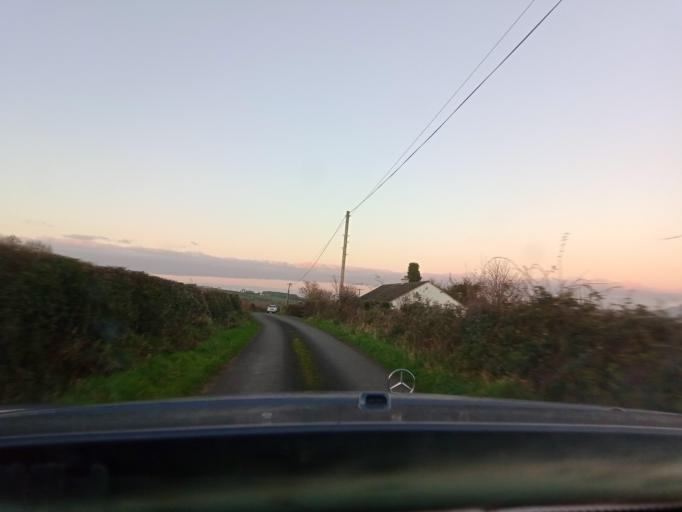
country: IE
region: Leinster
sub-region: Kilkenny
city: Graiguenamanagh
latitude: 52.5612
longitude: -6.9622
